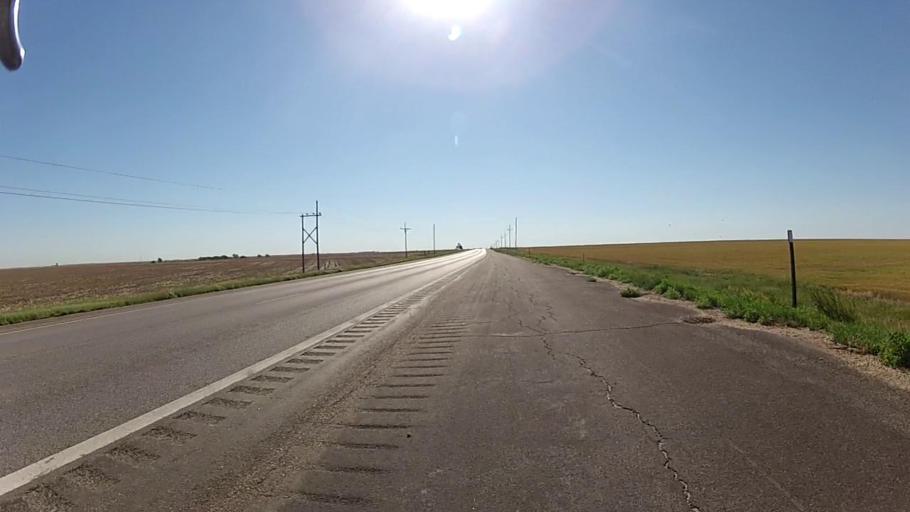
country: US
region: Kansas
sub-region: Ford County
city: Dodge City
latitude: 37.5863
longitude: -99.6785
